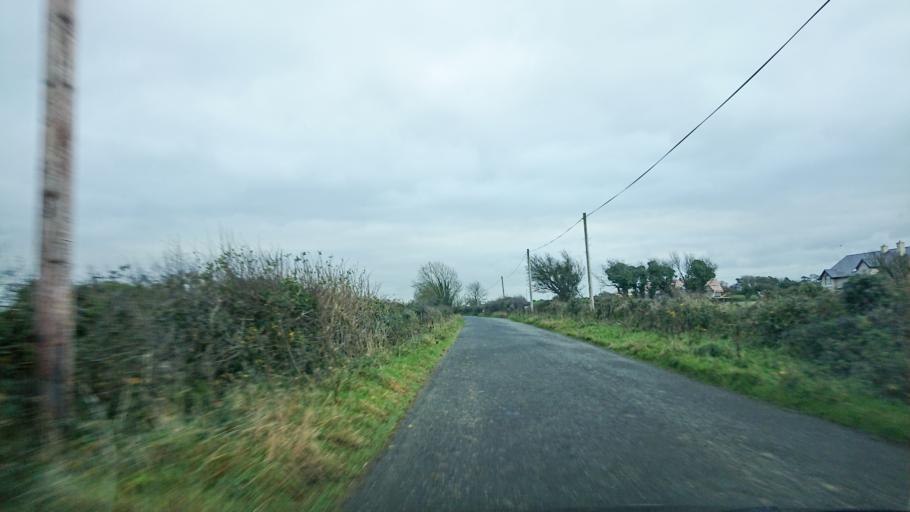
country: IE
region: Munster
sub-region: Waterford
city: Dunmore East
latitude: 52.2405
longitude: -6.9941
